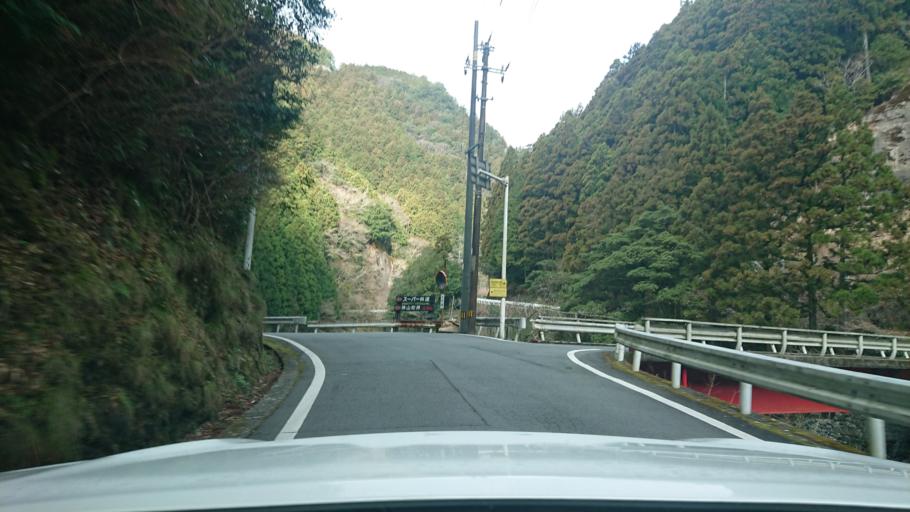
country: JP
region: Tokushima
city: Ishii
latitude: 33.9063
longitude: 134.3962
